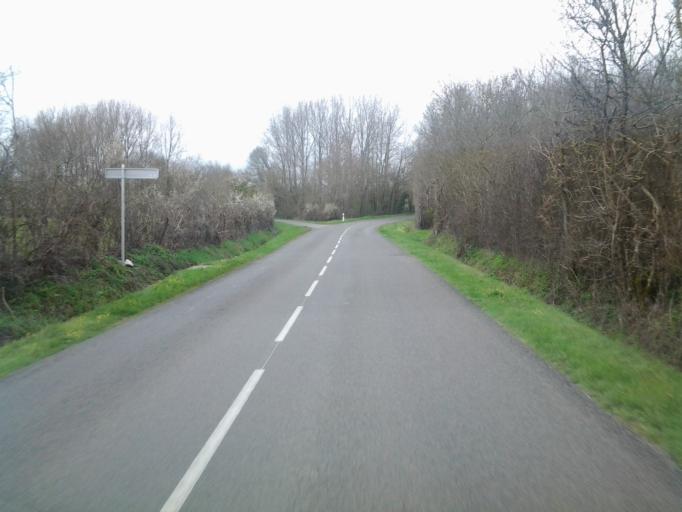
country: FR
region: Pays de la Loire
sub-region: Departement de la Vendee
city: Avrille
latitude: 46.4461
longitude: -1.4845
